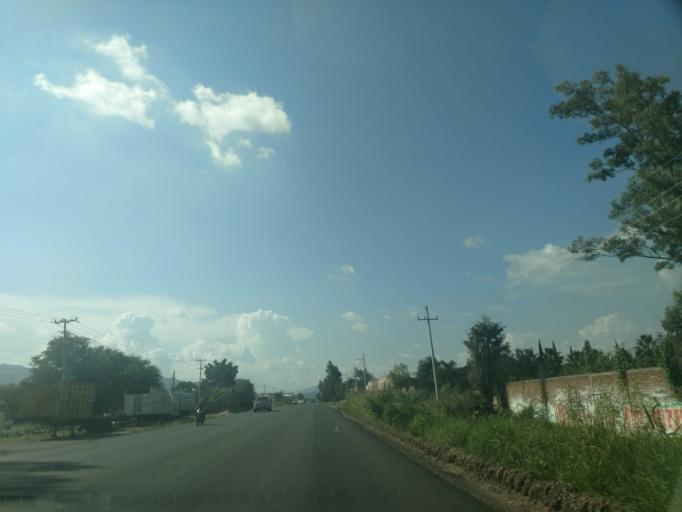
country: MX
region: Jalisco
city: Ahualulco de Mercado
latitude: 20.6987
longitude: -103.9649
